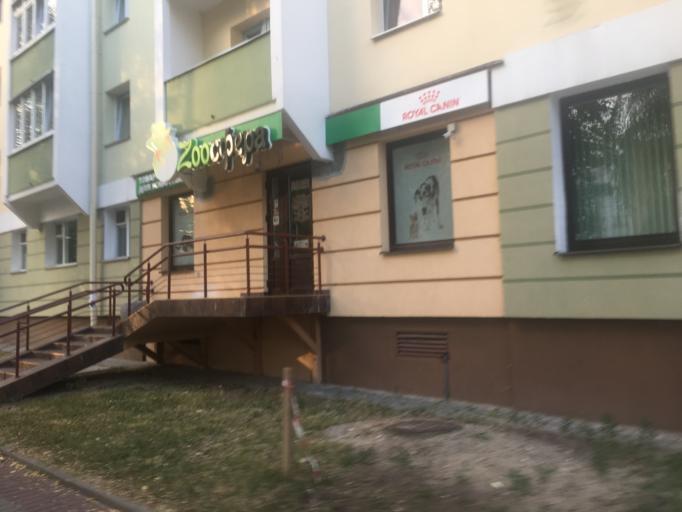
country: BY
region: Grodnenskaya
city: Hrodna
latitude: 53.6957
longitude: 23.8218
